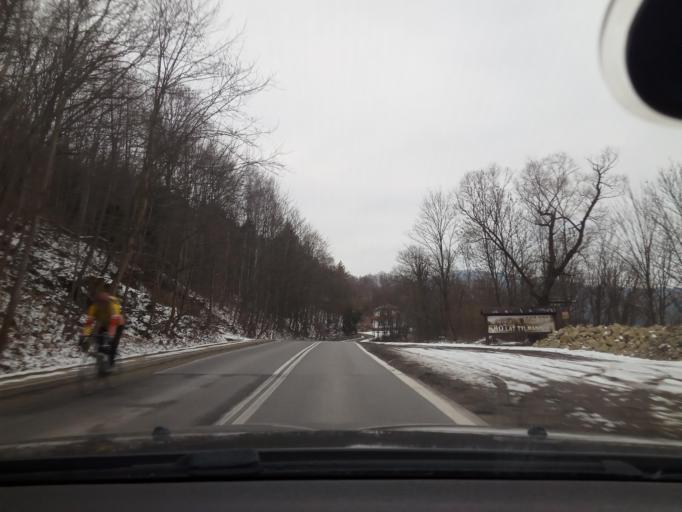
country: PL
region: Lesser Poland Voivodeship
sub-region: Powiat nowotarski
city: Kroscienko nad Dunajcem
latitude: 49.4753
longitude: 20.4205
